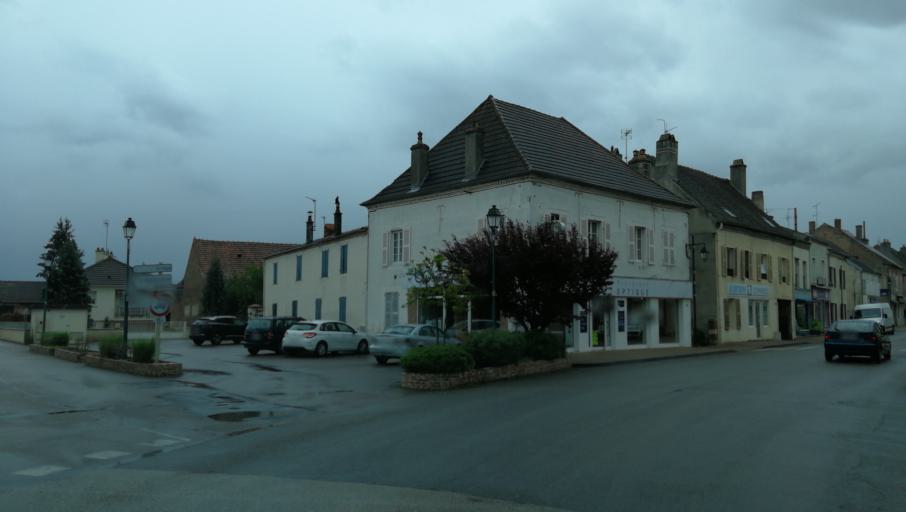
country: FR
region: Bourgogne
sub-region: Departement de Saone-et-Loire
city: Pierre-de-Bresse
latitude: 46.8862
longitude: 5.2612
